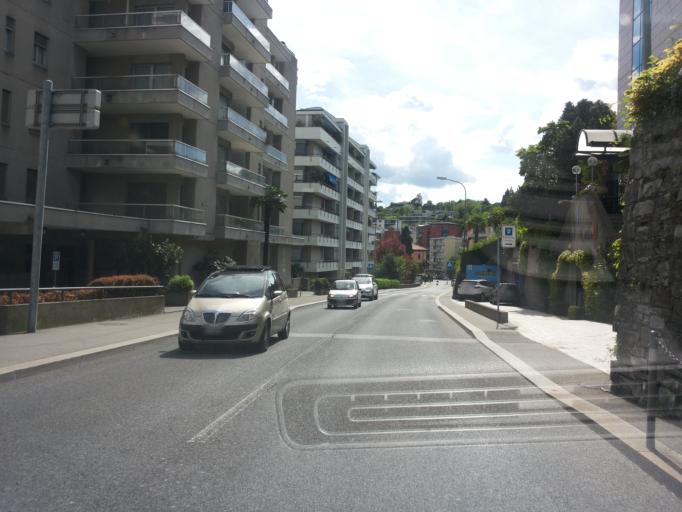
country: CH
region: Ticino
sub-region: Lugano District
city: Sorengo
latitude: 45.9995
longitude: 8.9462
